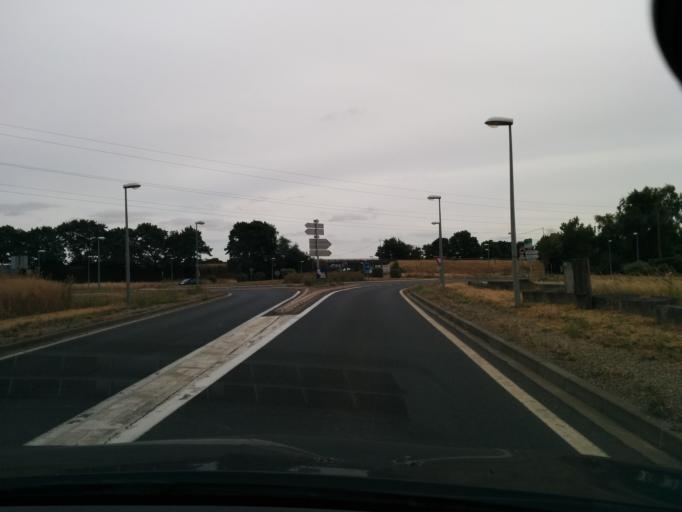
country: FR
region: Ile-de-France
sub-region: Departement de l'Essonne
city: Angerville
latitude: 48.3190
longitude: 1.9962
